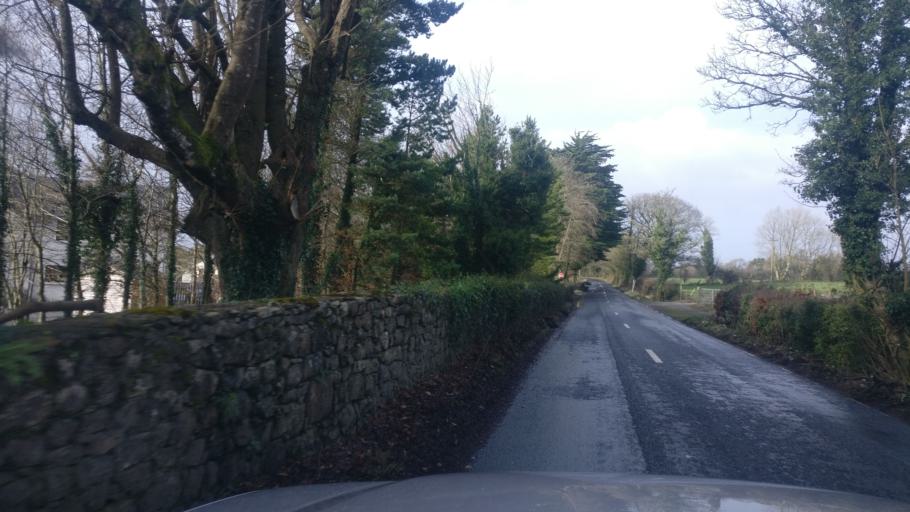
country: IE
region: Connaught
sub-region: County Galway
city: Loughrea
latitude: 53.2854
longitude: -8.5941
